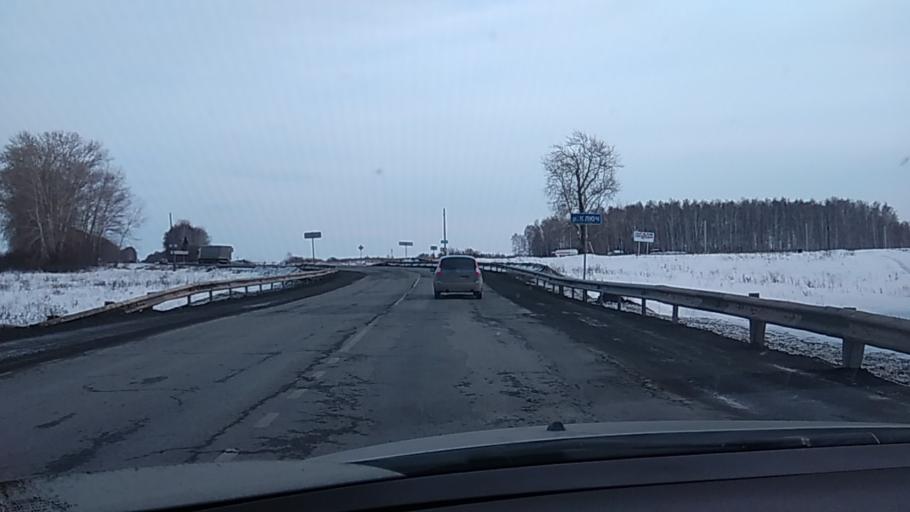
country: RU
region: Sverdlovsk
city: Pokrovskoye
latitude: 56.4688
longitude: 61.6719
